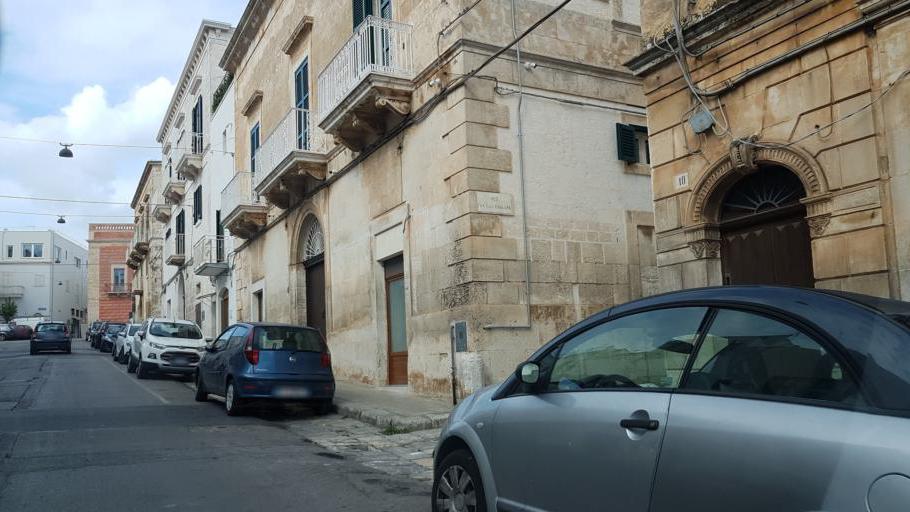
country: IT
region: Apulia
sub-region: Provincia di Brindisi
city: Ostuni
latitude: 40.7295
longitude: 17.5780
